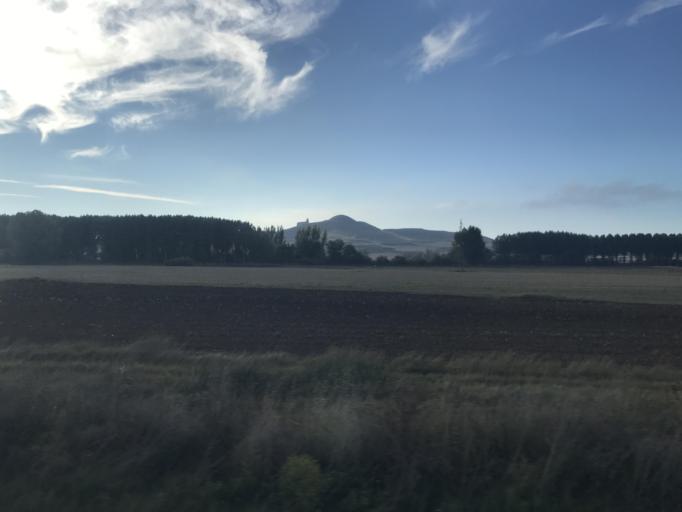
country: ES
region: Castille and Leon
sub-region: Provincia de Burgos
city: Estepar
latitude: 42.2661
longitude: -3.9094
